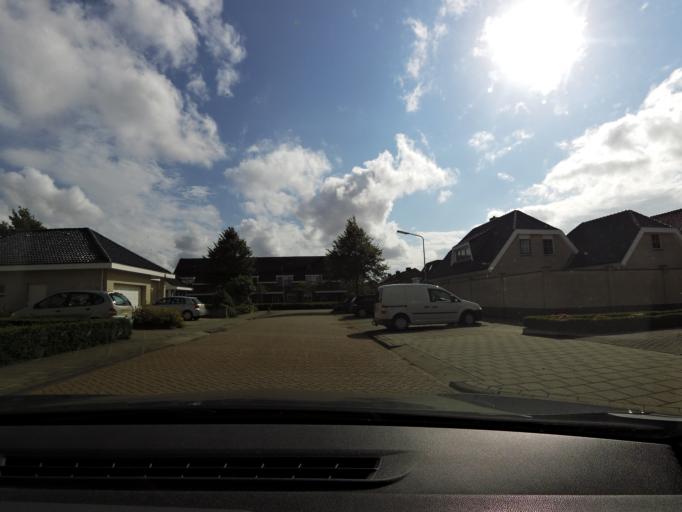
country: NL
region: South Holland
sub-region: Gemeente Goeree-Overflakkee
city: Goedereede
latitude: 51.8207
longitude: 3.9839
